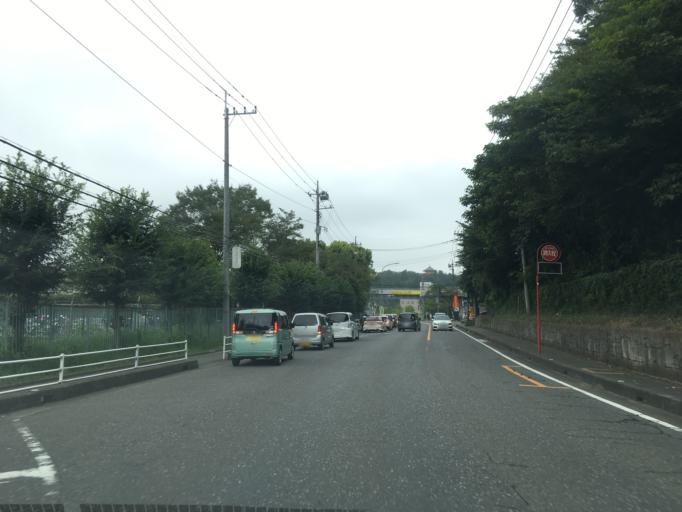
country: JP
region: Tokyo
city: Higashimurayama-shi
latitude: 35.7733
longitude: 139.4222
